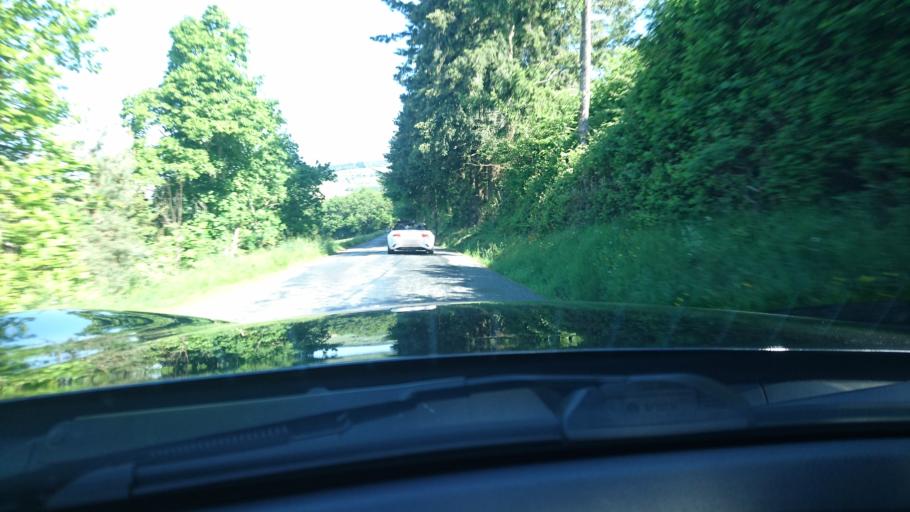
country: FR
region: Rhone-Alpes
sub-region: Departement de la Loire
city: Violay
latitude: 45.8211
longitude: 4.3848
